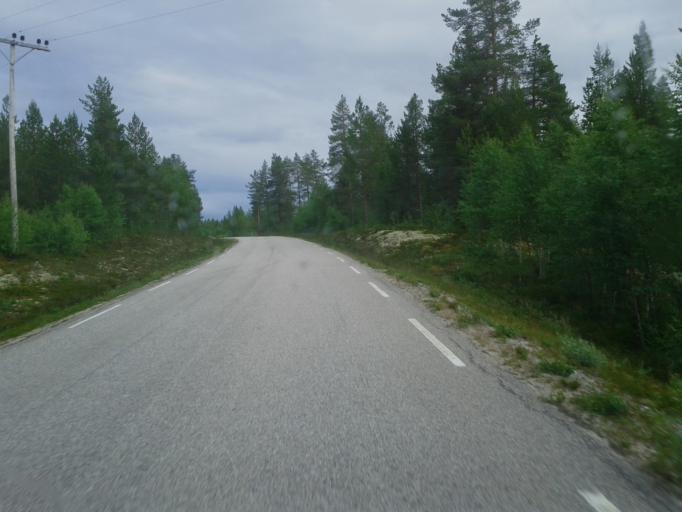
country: NO
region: Hedmark
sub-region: Engerdal
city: Engerdal
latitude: 62.0505
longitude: 11.6878
